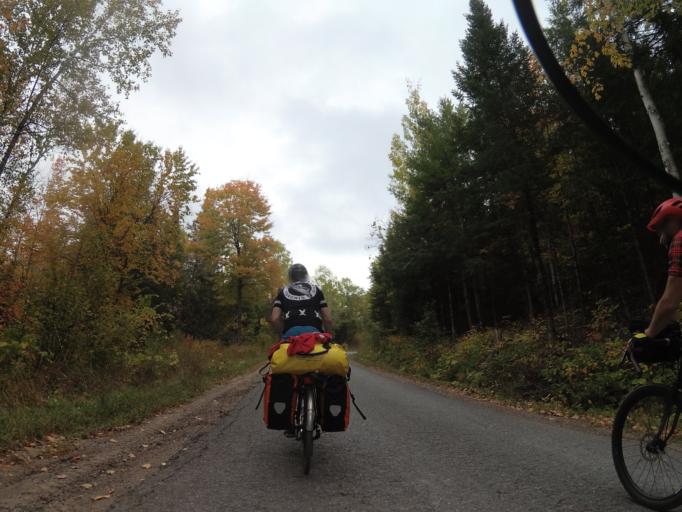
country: CA
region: Ontario
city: Renfrew
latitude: 45.2515
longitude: -77.1887
